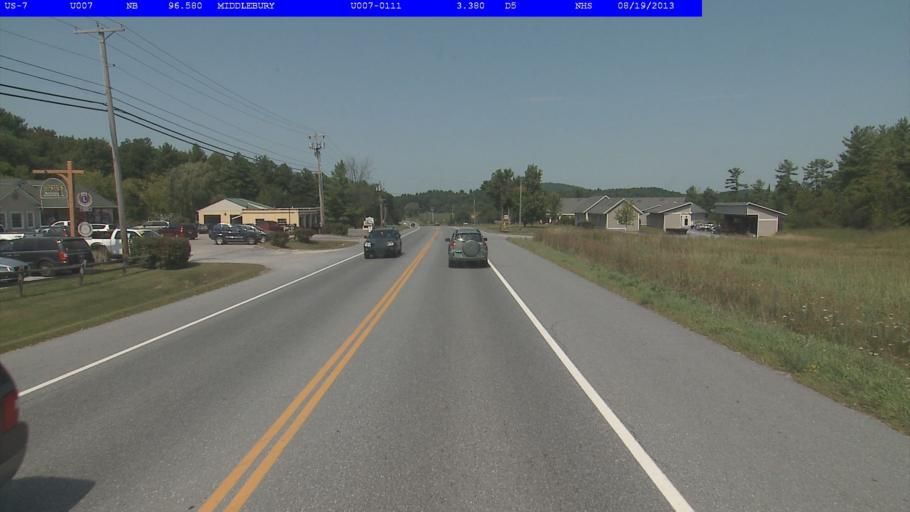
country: US
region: Vermont
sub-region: Addison County
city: Middlebury (village)
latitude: 43.9966
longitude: -73.1452
